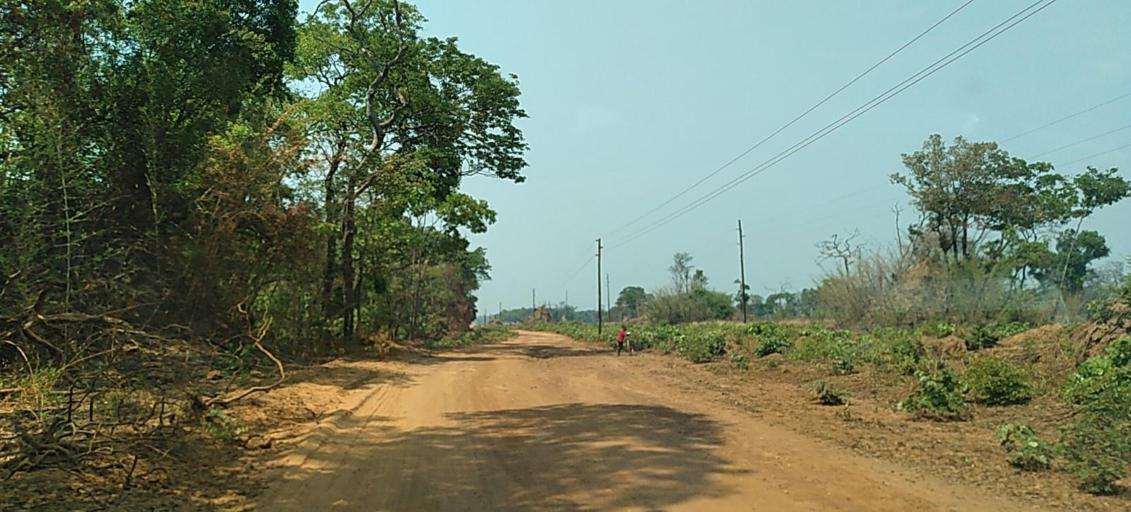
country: ZM
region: Copperbelt
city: Kalulushi
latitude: -13.0872
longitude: 27.4088
